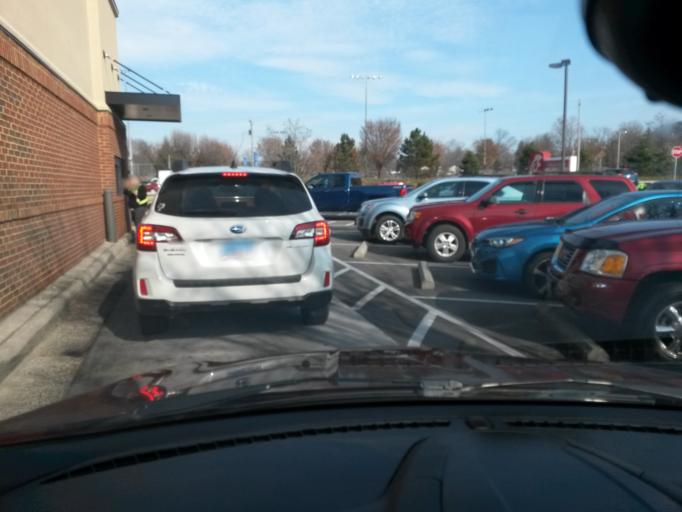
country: US
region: Virginia
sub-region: City of Roanoke
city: Roanoke
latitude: 37.3031
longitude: -79.9595
